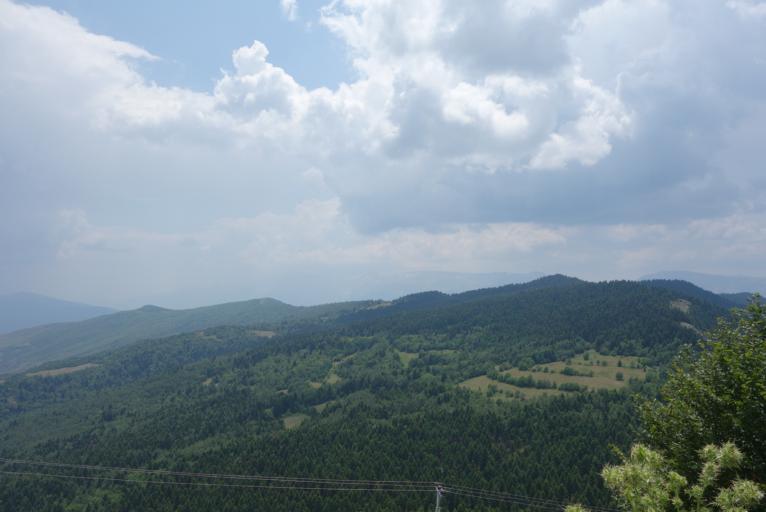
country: AL
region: Gjirokaster
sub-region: Rrethi i Permetit
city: Frasher
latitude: 40.3468
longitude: 20.4160
